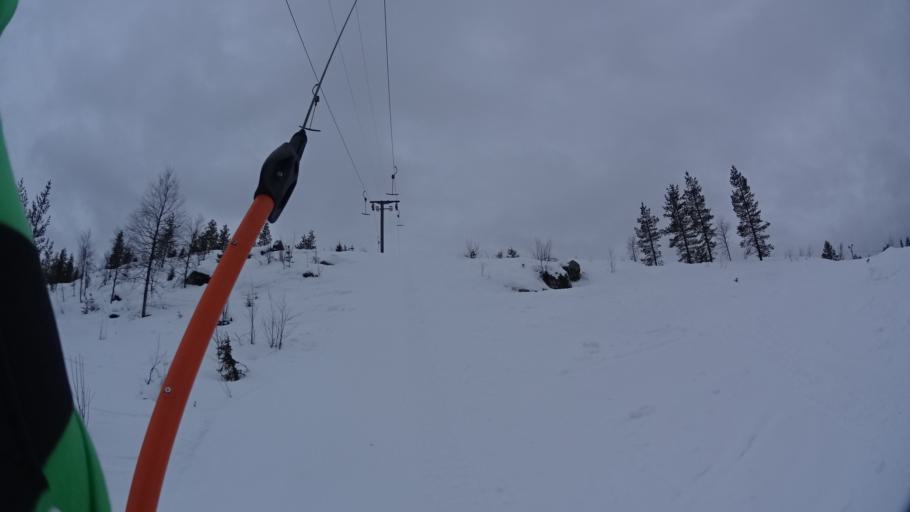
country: SE
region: Vaesterbotten
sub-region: Mala Kommun
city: Mala
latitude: 65.1789
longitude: 18.7678
